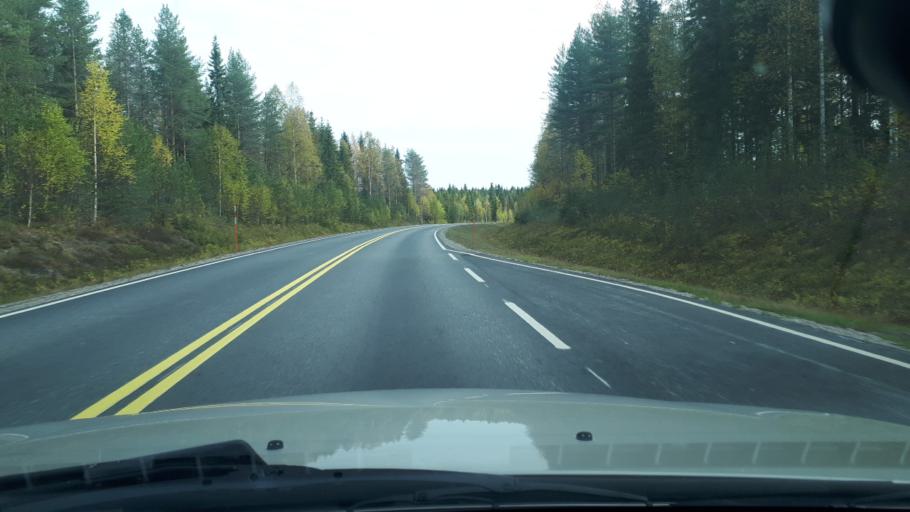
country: FI
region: Lapland
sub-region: Rovaniemi
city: Ranua
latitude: 65.9674
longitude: 26.0020
